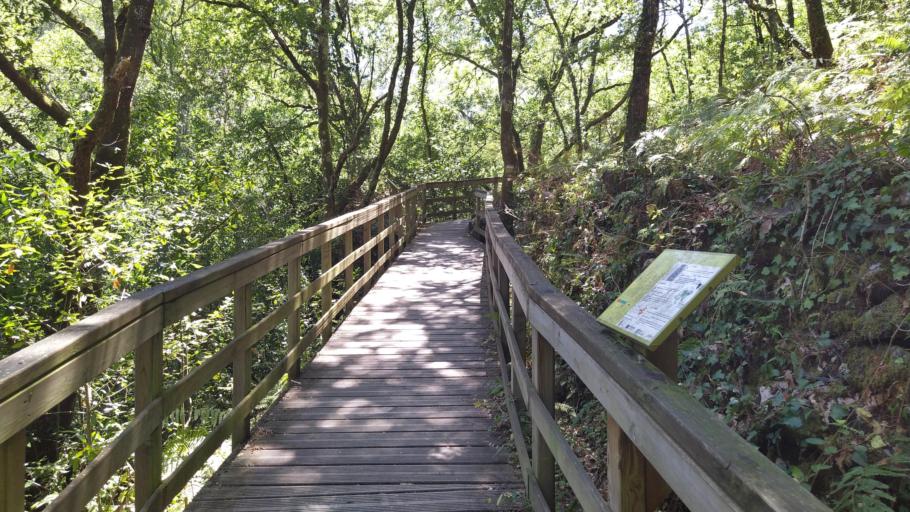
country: ES
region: Galicia
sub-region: Provincia de Lugo
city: Lobios
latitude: 42.3765
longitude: -7.4973
